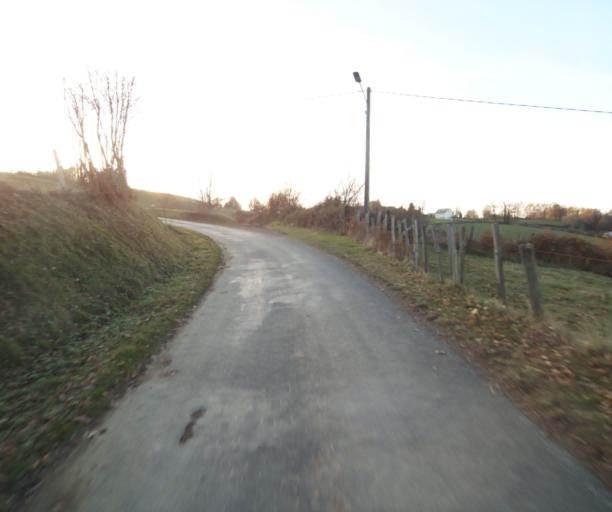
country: FR
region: Limousin
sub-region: Departement de la Correze
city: Laguenne
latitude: 45.2369
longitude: 1.8234
